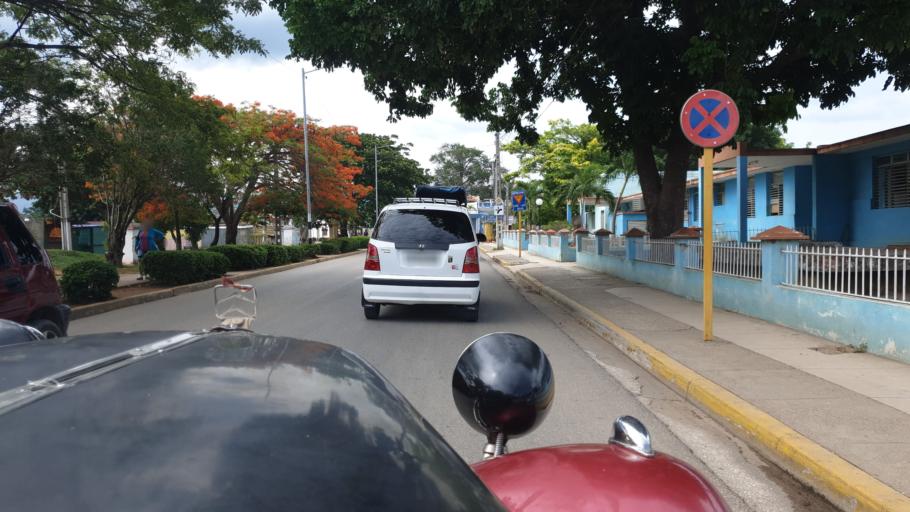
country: CU
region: Sancti Spiritus
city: Trinidad
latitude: 21.7960
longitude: -79.9865
